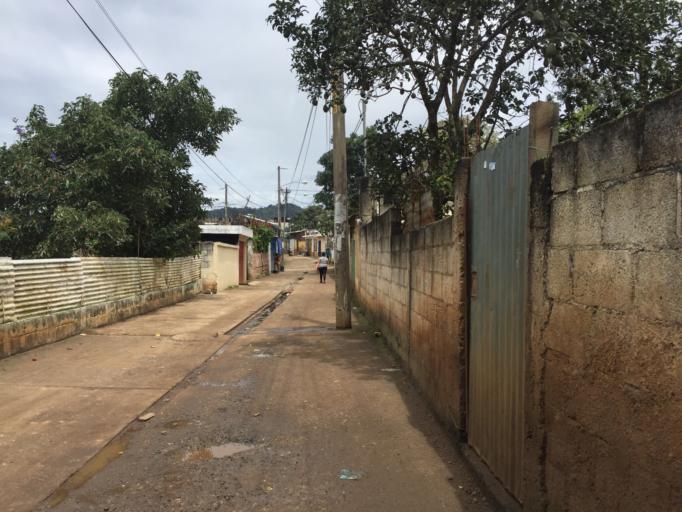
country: GT
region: Guatemala
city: Villa Canales
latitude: 14.4791
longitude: -90.5234
